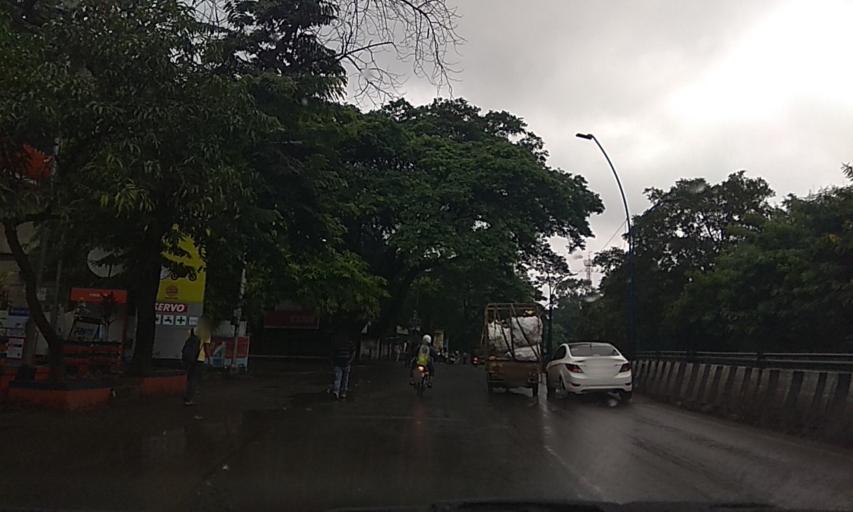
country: IN
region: Maharashtra
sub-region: Pune Division
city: Shivaji Nagar
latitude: 18.5280
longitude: 73.8504
